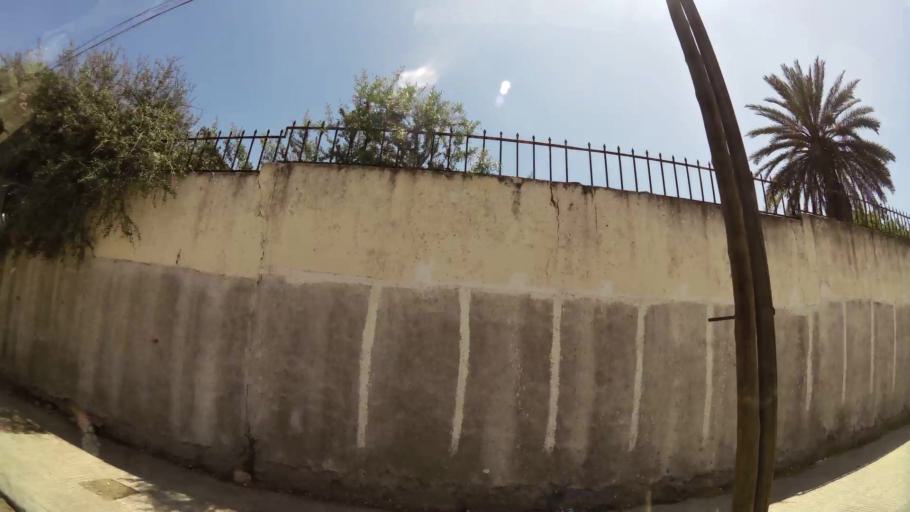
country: MA
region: Gharb-Chrarda-Beni Hssen
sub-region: Kenitra Province
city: Kenitra
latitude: 34.2593
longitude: -6.5609
